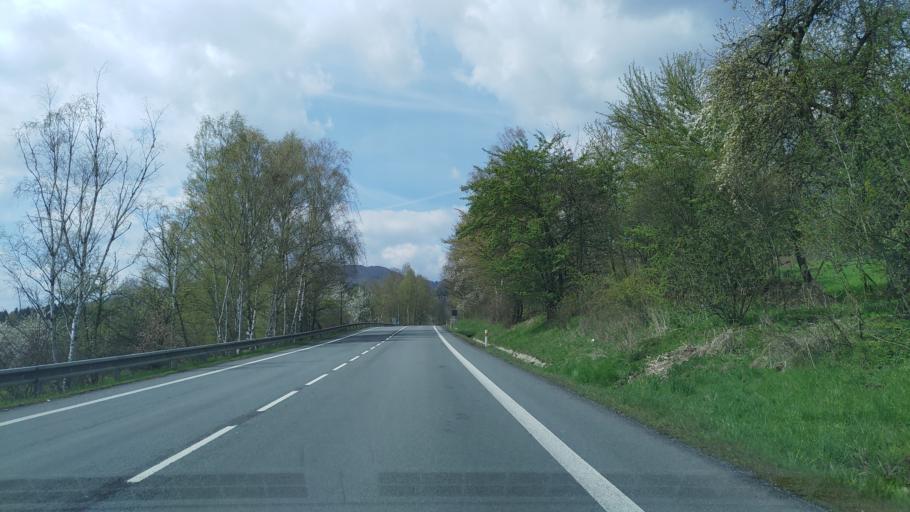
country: CZ
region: Ustecky
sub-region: Okres Chomutov
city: Perstejn
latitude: 50.3736
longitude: 13.0959
